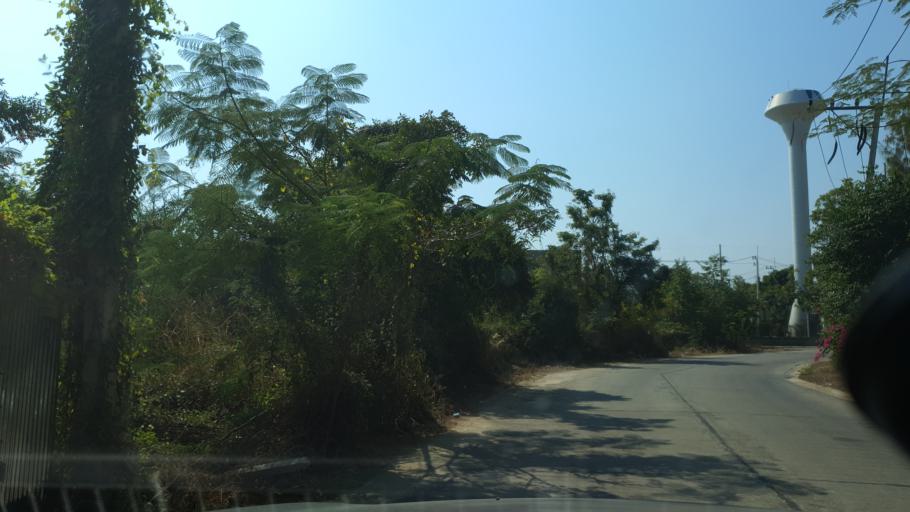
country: TH
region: Phetchaburi
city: Cha-am
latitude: 12.7808
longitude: 99.9769
